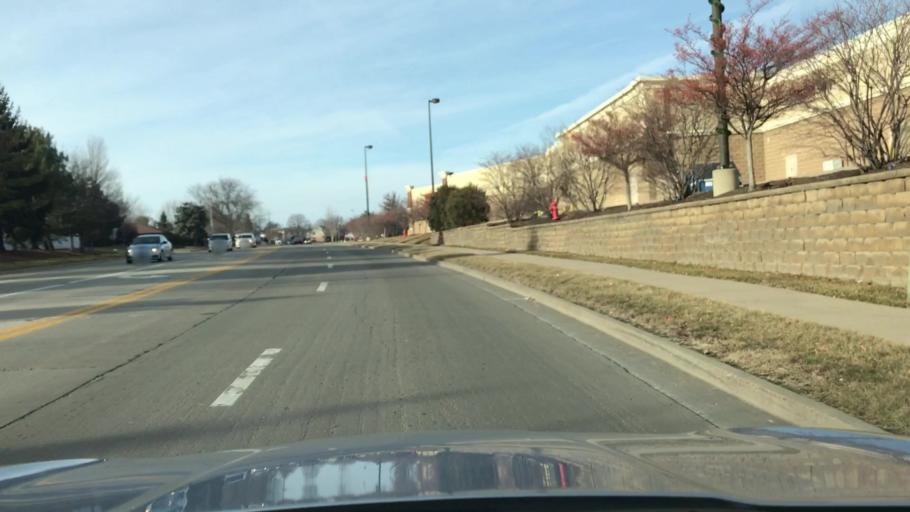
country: US
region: Illinois
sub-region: McLean County
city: Normal
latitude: 40.5053
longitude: -88.9579
